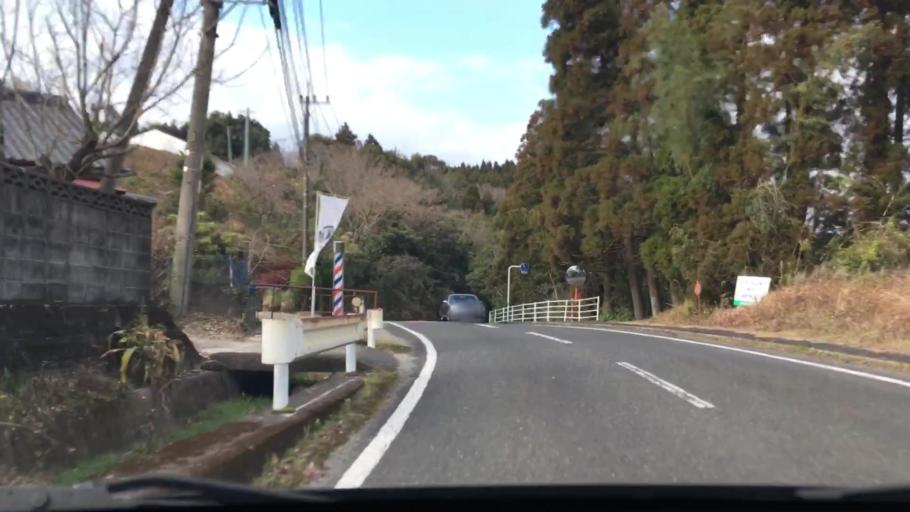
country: JP
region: Miyazaki
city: Kushima
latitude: 31.5415
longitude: 131.2423
